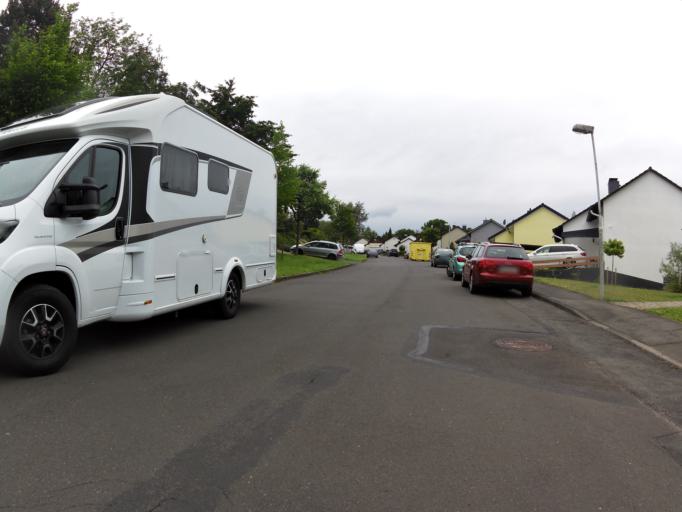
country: DE
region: Hesse
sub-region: Regierungsbezirk Kassel
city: Bad Hersfeld
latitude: 50.8667
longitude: 9.6779
